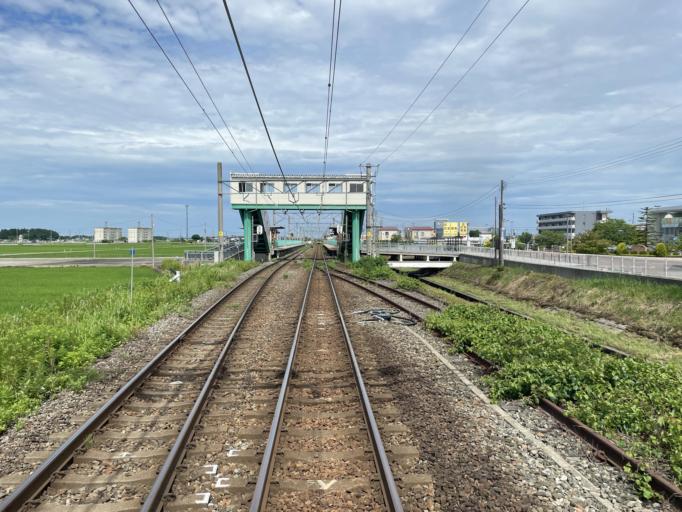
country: JP
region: Niigata
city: Shibata
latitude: 37.9413
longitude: 139.3076
